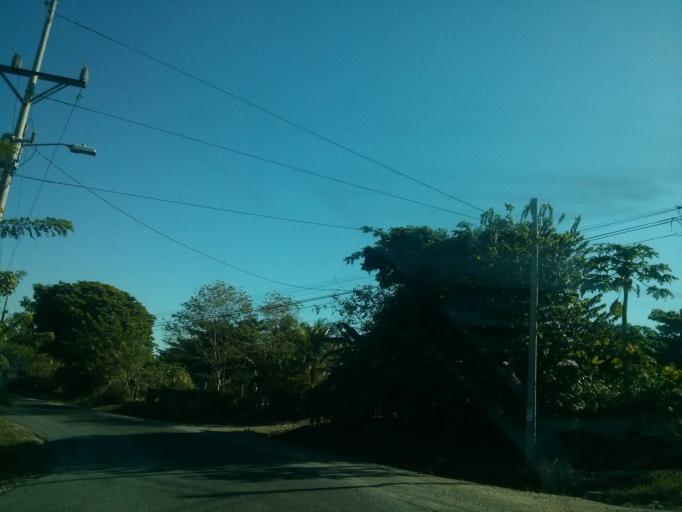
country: CR
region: Puntarenas
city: Paquera
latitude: 9.6579
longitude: -85.1210
